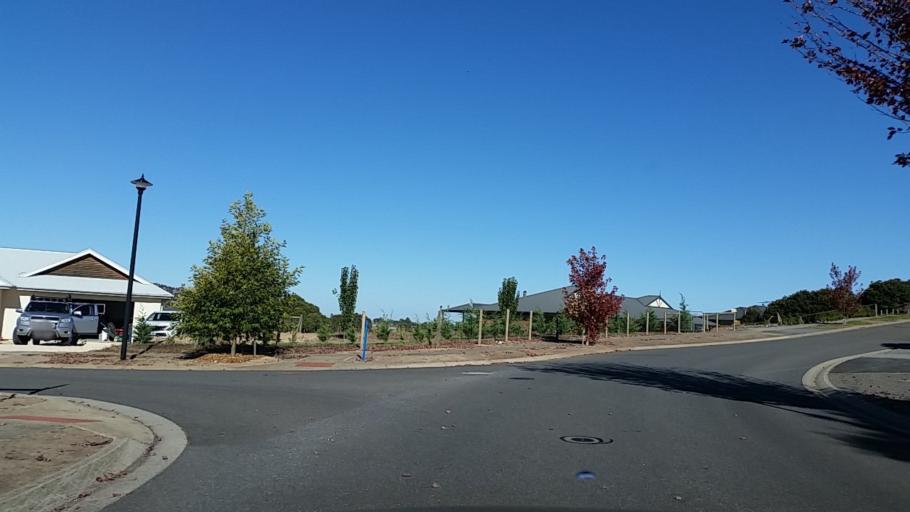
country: AU
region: South Australia
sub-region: Mount Barker
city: Mount Barker
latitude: -35.0593
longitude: 138.8857
